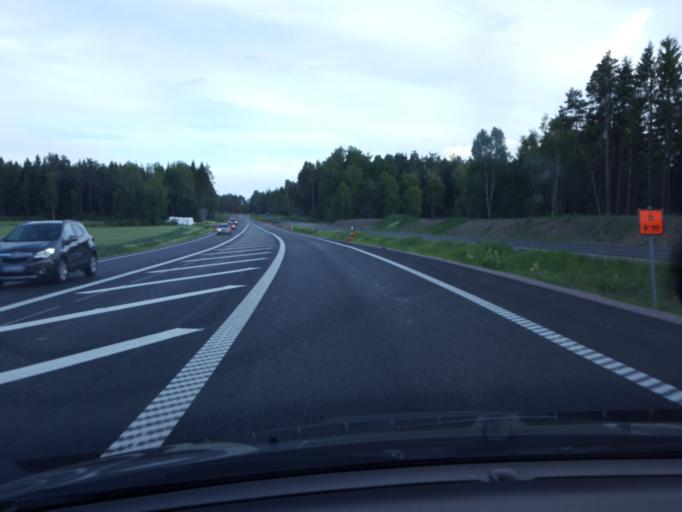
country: SE
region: Uppsala
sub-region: Osthammars Kommun
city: Gimo
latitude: 60.1061
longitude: 18.1249
